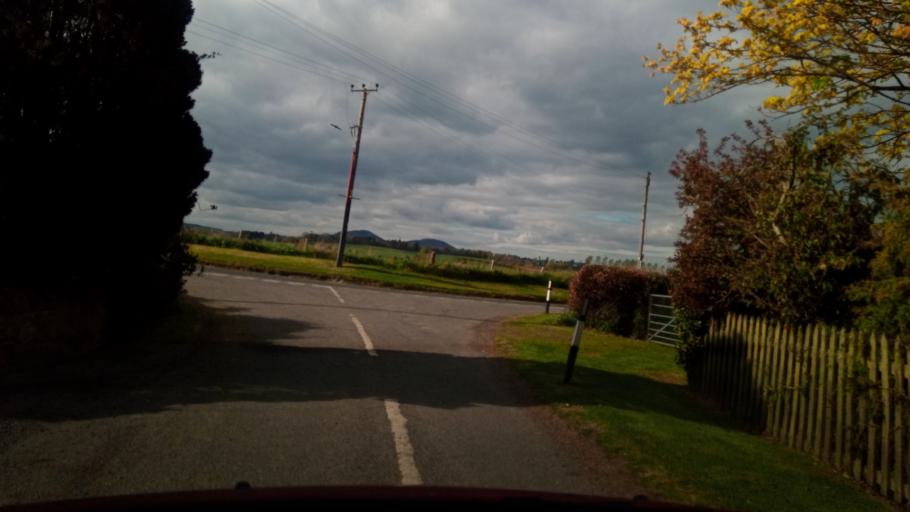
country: GB
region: Scotland
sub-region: The Scottish Borders
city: Saint Boswells
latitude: 55.5167
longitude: -2.6798
